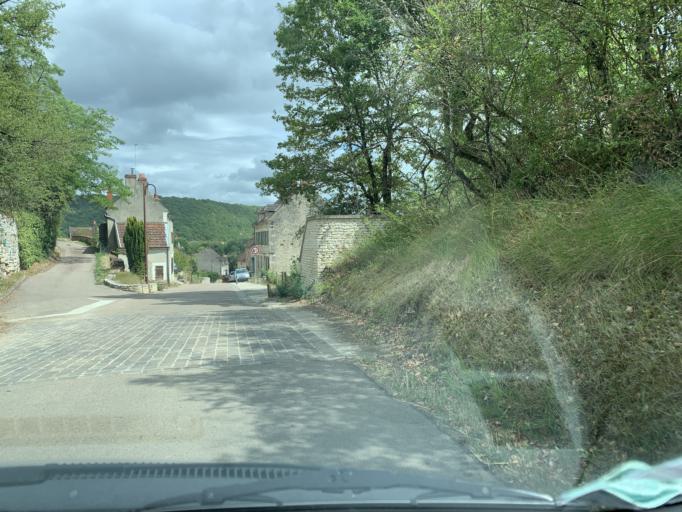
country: FR
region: Bourgogne
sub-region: Departement de la Nievre
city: Clamecy
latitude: 47.4491
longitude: 3.5424
